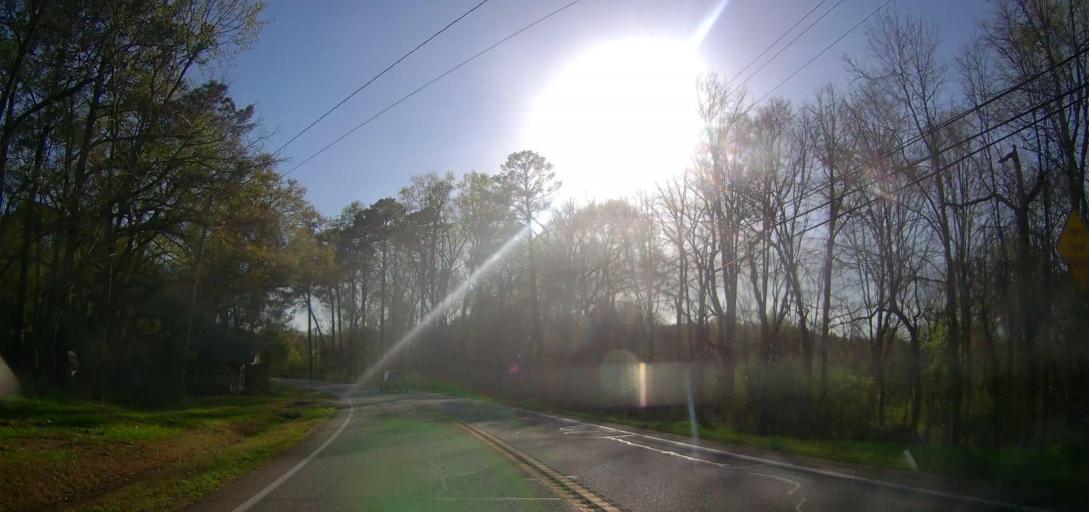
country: US
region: Georgia
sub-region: Butts County
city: Indian Springs
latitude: 33.2513
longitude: -83.9187
